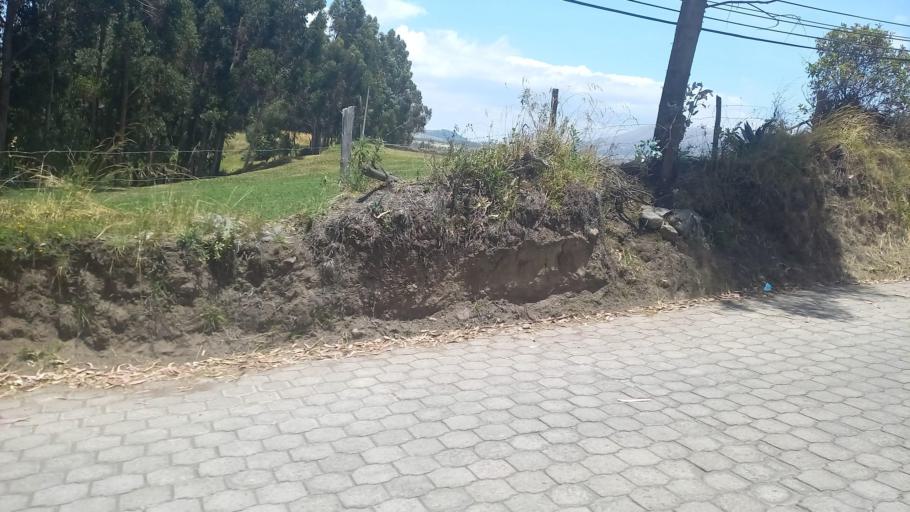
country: EC
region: Pichincha
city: Cayambe
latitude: 0.1395
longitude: -78.0673
